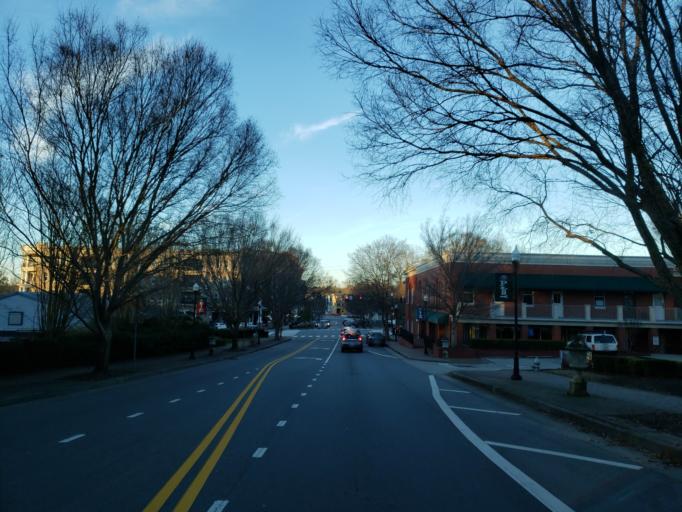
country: US
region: Georgia
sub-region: Fulton County
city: Alpharetta
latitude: 34.0748
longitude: -84.2965
